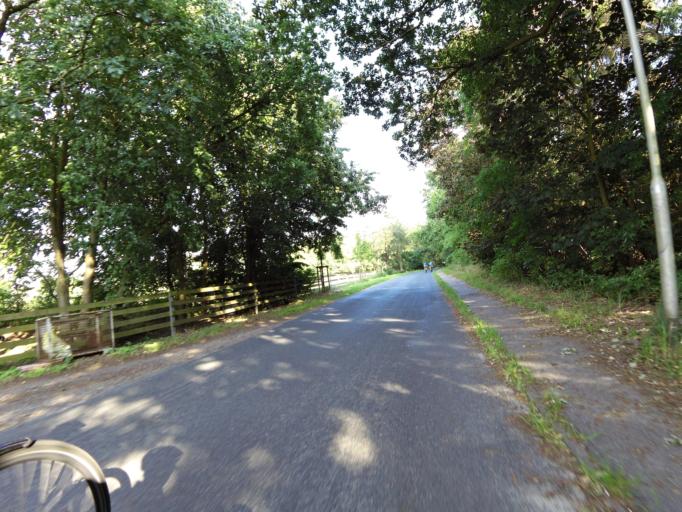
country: DE
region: Lower Saxony
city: Nordholz
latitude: 53.8265
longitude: 8.5852
